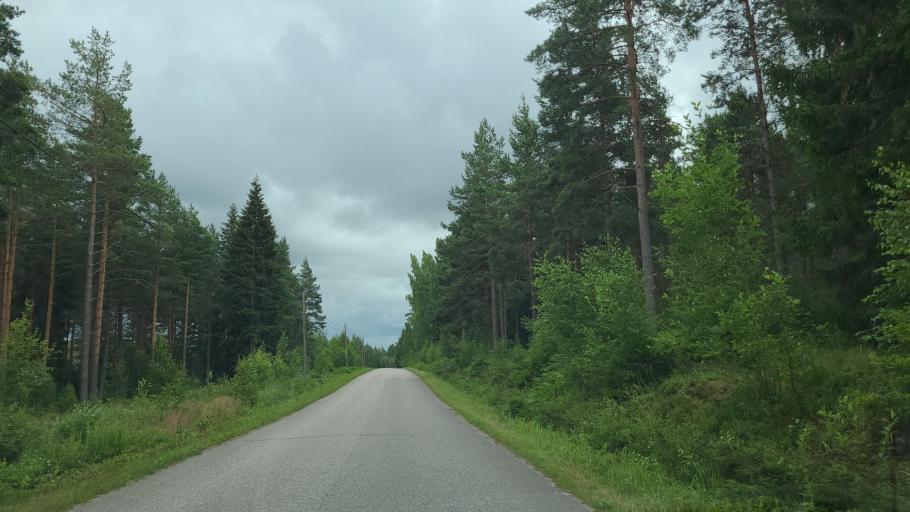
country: FI
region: Varsinais-Suomi
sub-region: Aboland-Turunmaa
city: Dragsfjaerd
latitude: 60.0784
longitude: 22.4258
